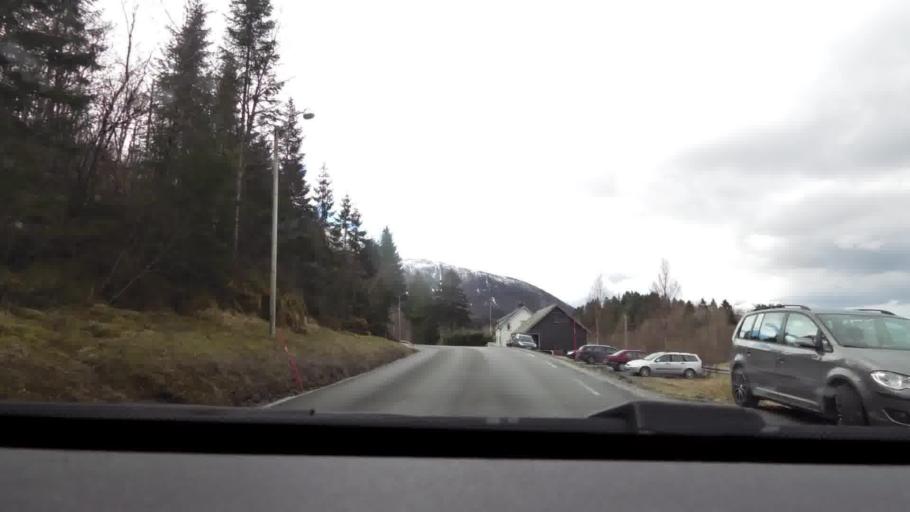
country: NO
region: More og Romsdal
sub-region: Kristiansund
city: Rensvik
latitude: 63.1111
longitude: 7.7904
